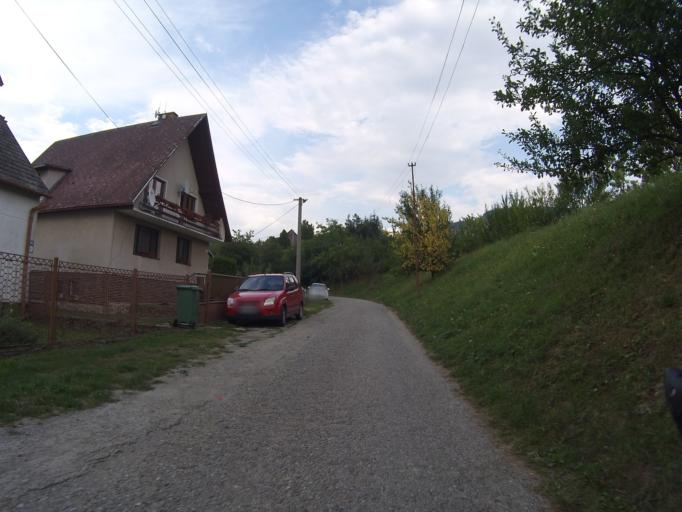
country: SK
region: Nitriansky
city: Ilava
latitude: 49.0383
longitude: 18.3123
